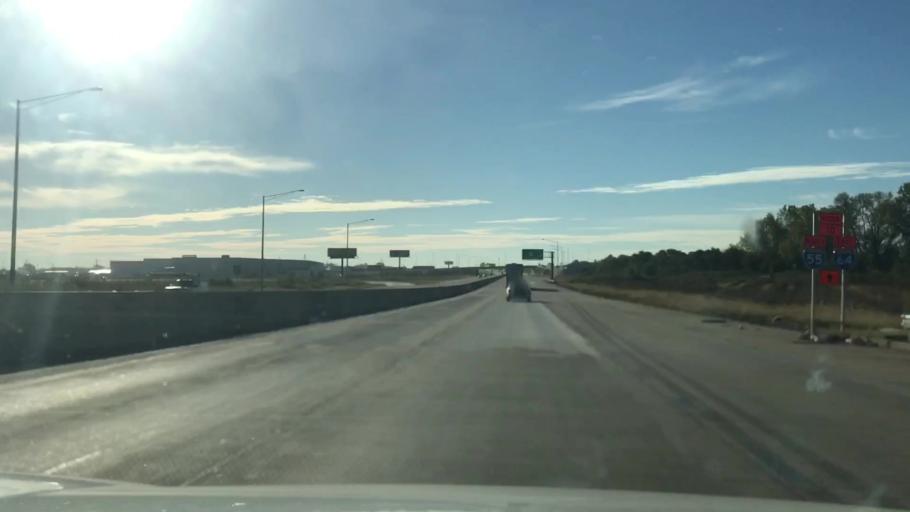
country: US
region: Illinois
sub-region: Saint Clair County
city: East Saint Louis
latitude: 38.6469
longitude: -90.1589
